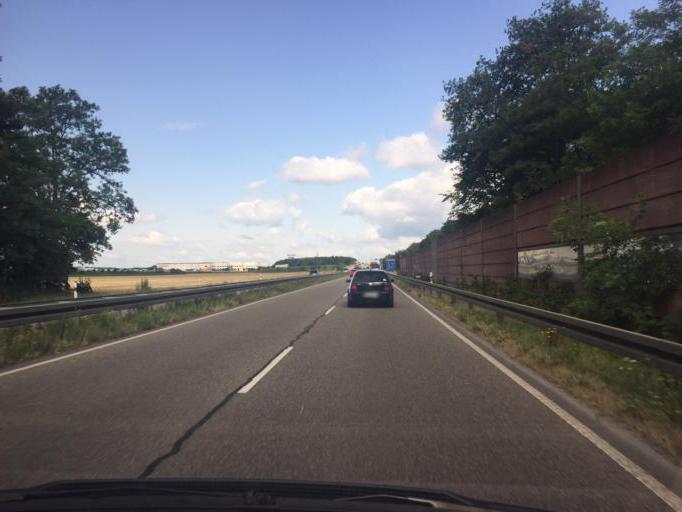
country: DE
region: Baden-Wuerttemberg
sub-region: Karlsruhe Region
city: Forst
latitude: 49.1452
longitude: 8.5708
